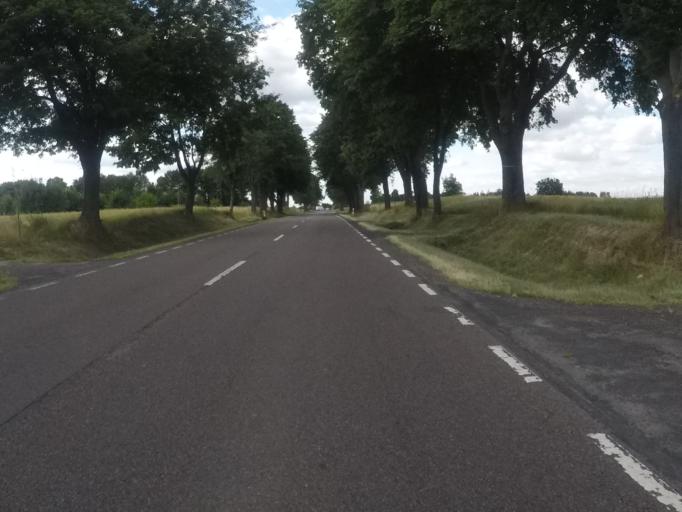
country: PL
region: Lublin Voivodeship
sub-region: Powiat krasnicki
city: Krasnik
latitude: 50.8779
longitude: 22.2647
